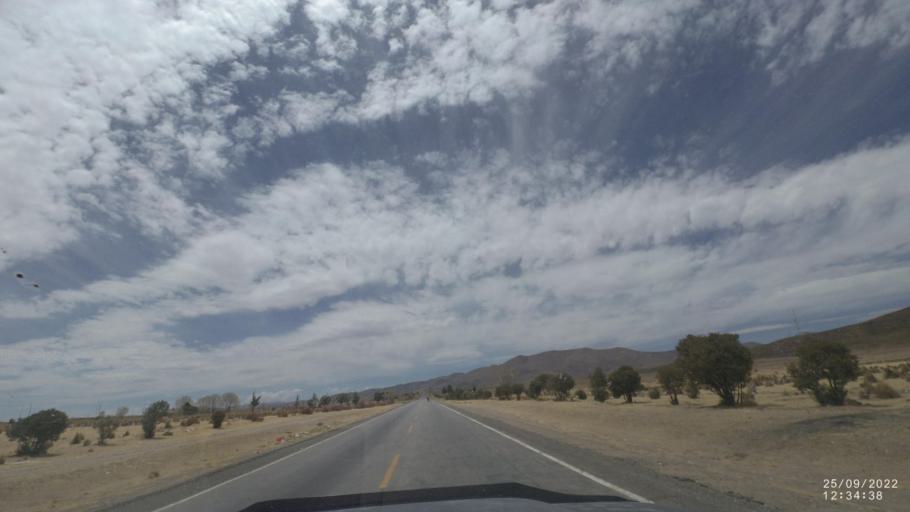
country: BO
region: Oruro
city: Machacamarca
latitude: -18.1728
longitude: -67.0130
